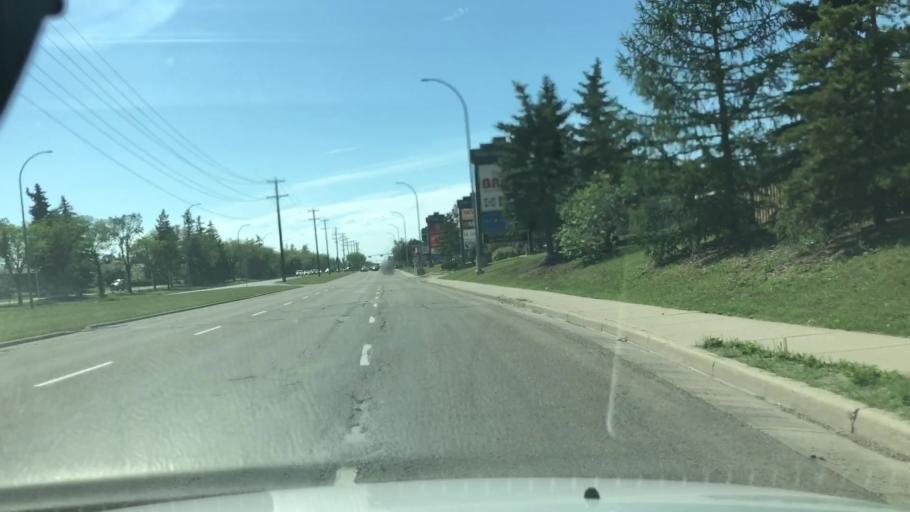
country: CA
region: Alberta
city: Edmonton
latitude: 53.5996
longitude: -113.5299
